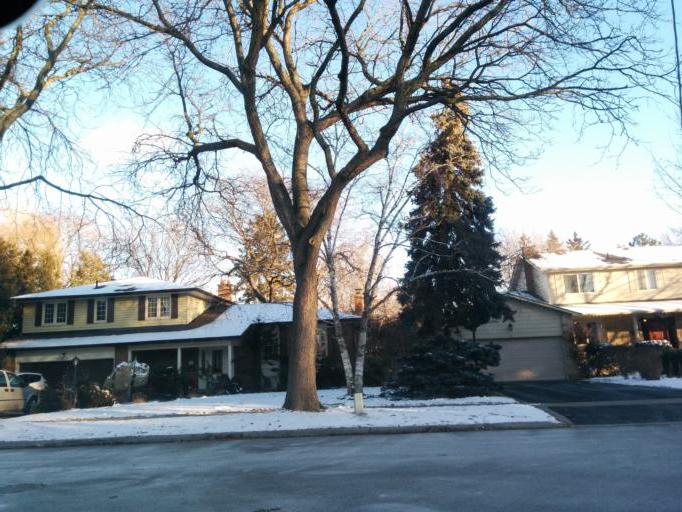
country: CA
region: Ontario
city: Mississauga
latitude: 43.5460
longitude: -79.6118
